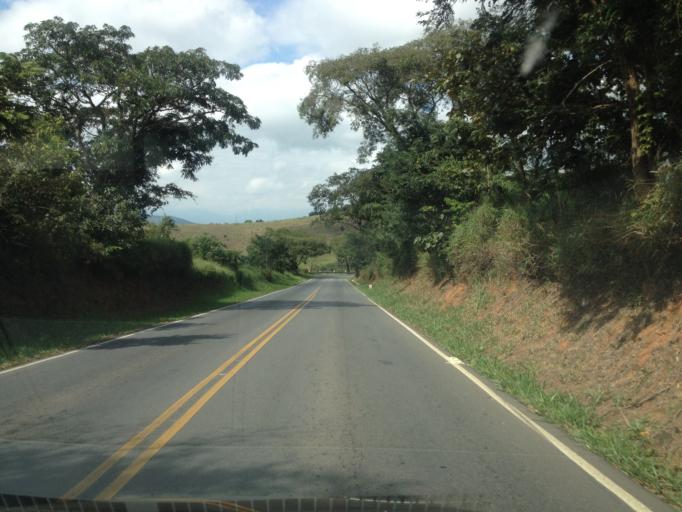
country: BR
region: Minas Gerais
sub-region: Itanhandu
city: Itanhandu
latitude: -22.2168
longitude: -44.9471
